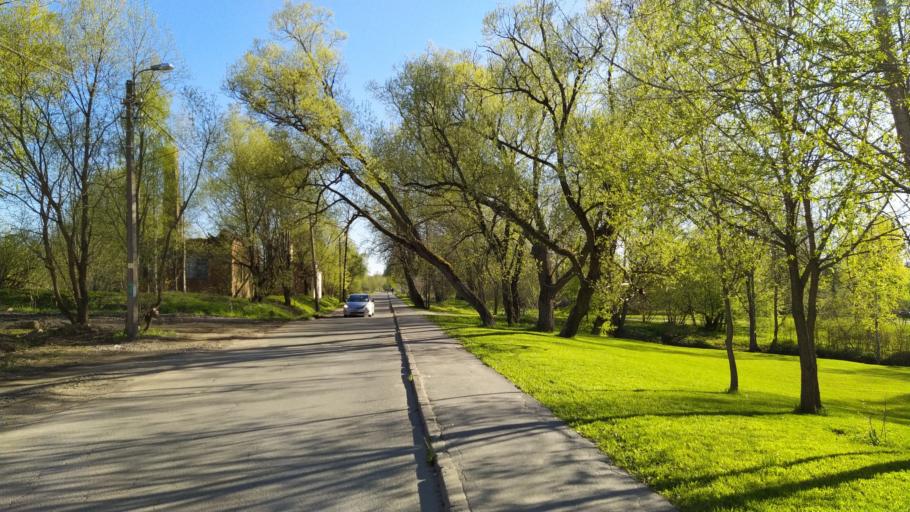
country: RU
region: St.-Petersburg
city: Pavlovsk
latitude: 59.6780
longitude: 30.4482
